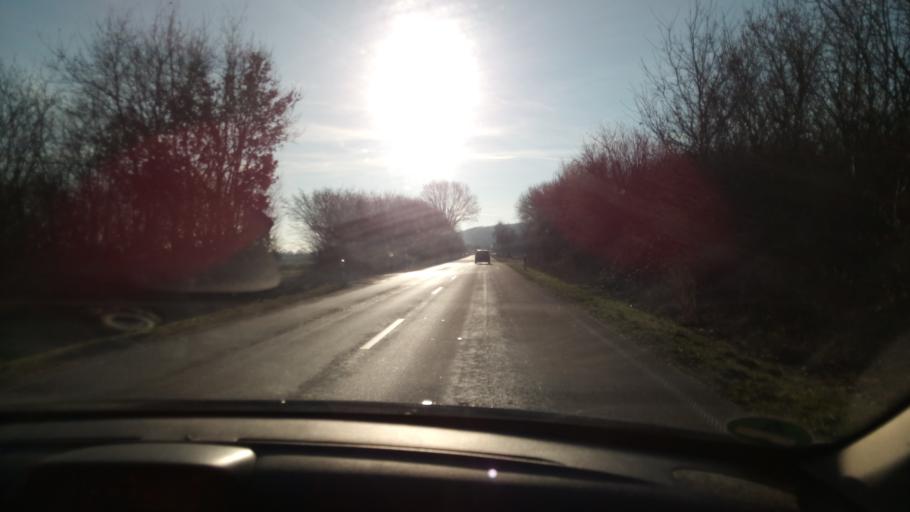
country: DE
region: Schleswig-Holstein
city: Dalldorf
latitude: 53.4333
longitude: 10.6025
